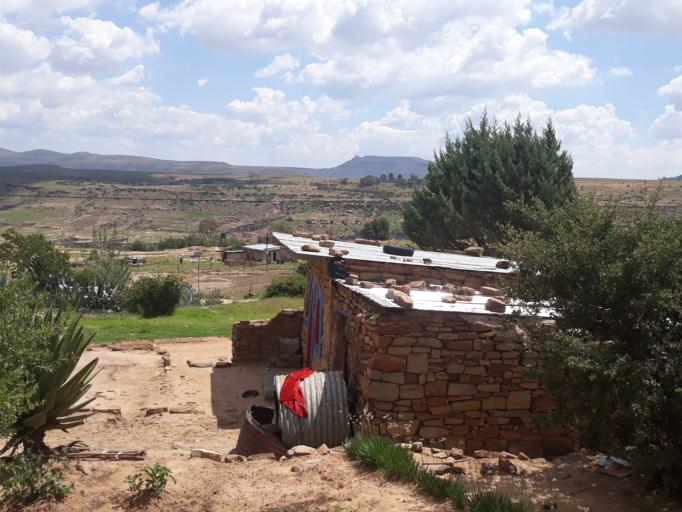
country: LS
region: Quthing
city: Quthing
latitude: -30.3431
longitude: 27.5305
